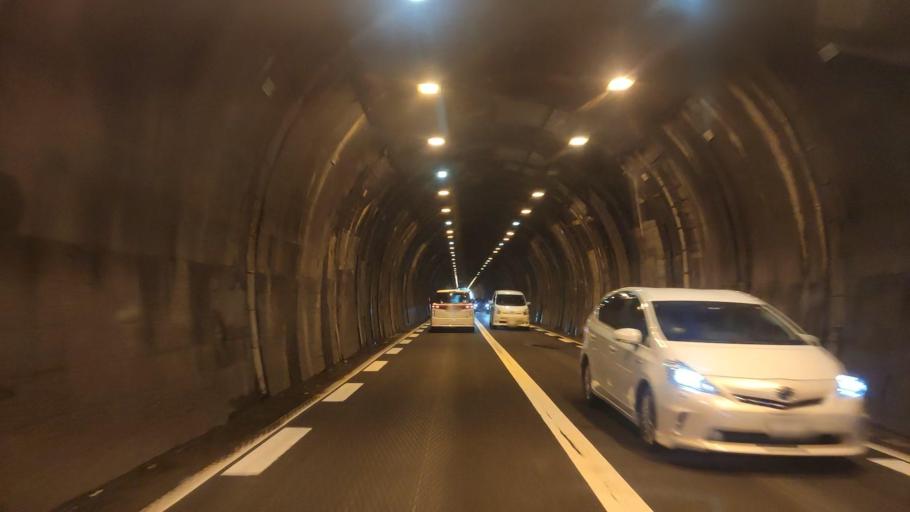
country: JP
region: Fukui
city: Takefu
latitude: 35.7837
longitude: 136.1012
